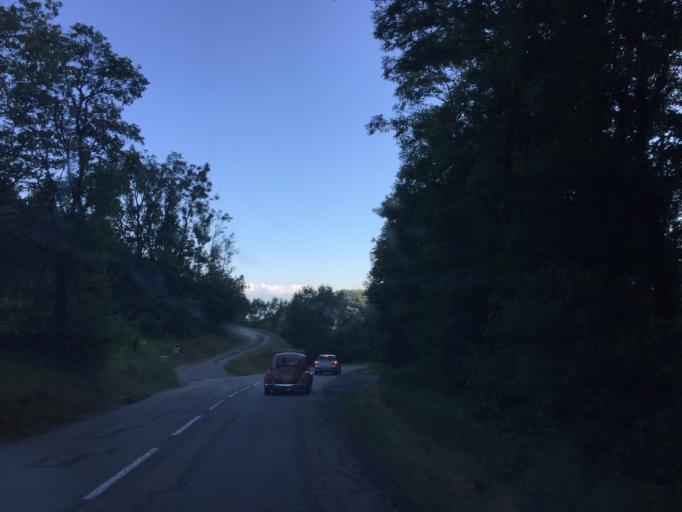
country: FR
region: Rhone-Alpes
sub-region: Departement de la Savoie
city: Challes-les-Eaux
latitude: 45.5461
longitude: 6.0057
